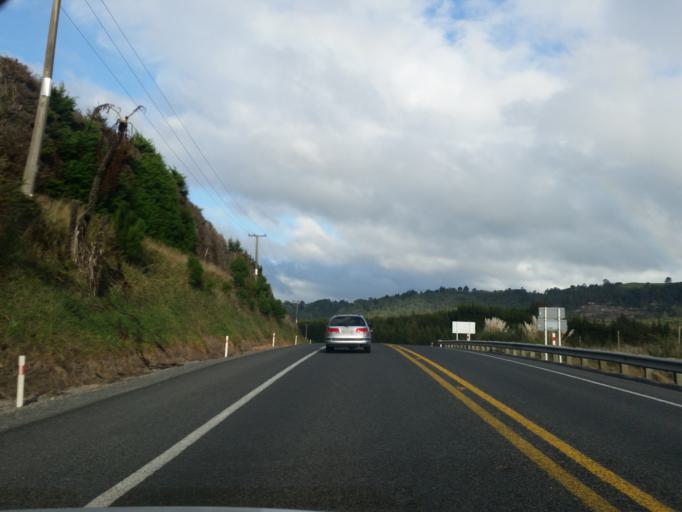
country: NZ
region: Bay of Plenty
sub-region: Tauranga City
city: Tauranga
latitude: -37.6889
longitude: 176.0405
